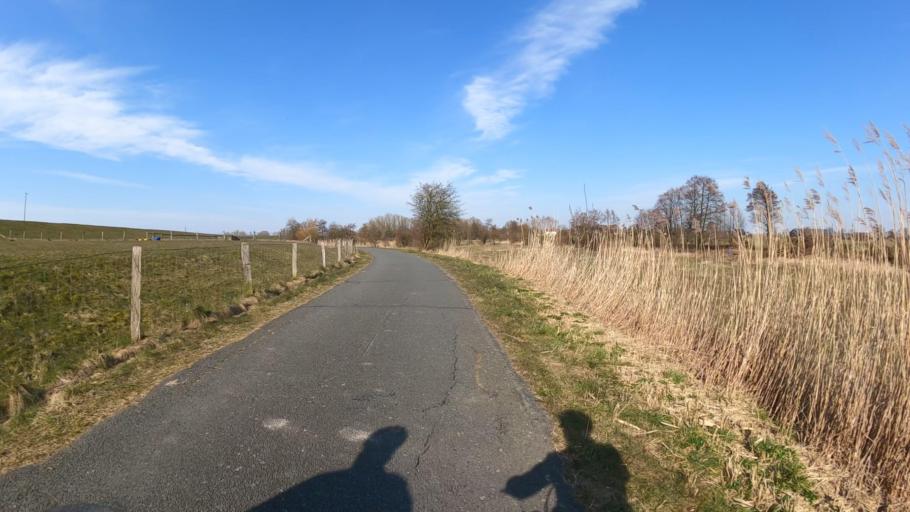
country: DE
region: Schleswig-Holstein
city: Haseldorf
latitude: 53.6438
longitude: 9.5632
